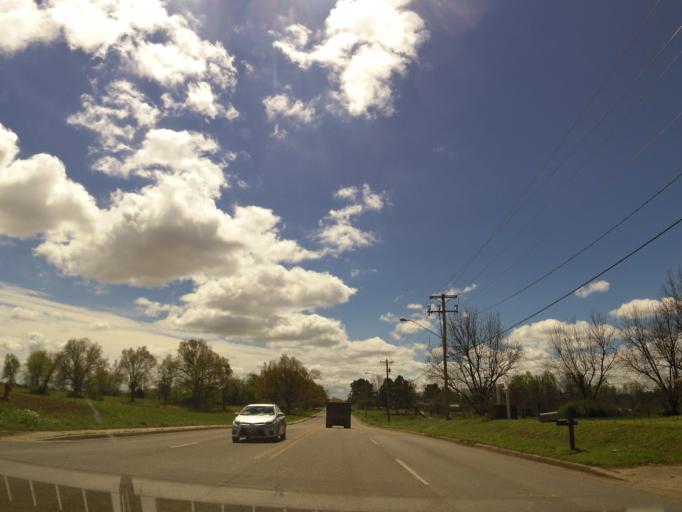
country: US
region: Arkansas
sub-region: Craighead County
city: Jonesboro
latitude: 35.8721
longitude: -90.7029
